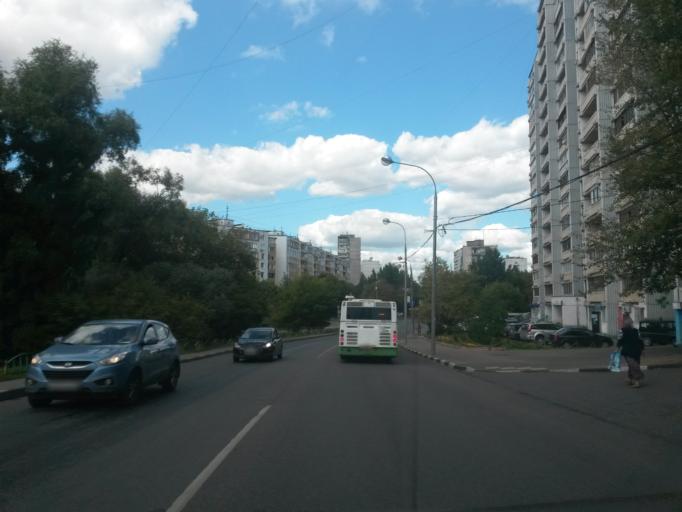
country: RU
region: Moscow
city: Mar'ino
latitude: 55.6759
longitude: 37.7229
